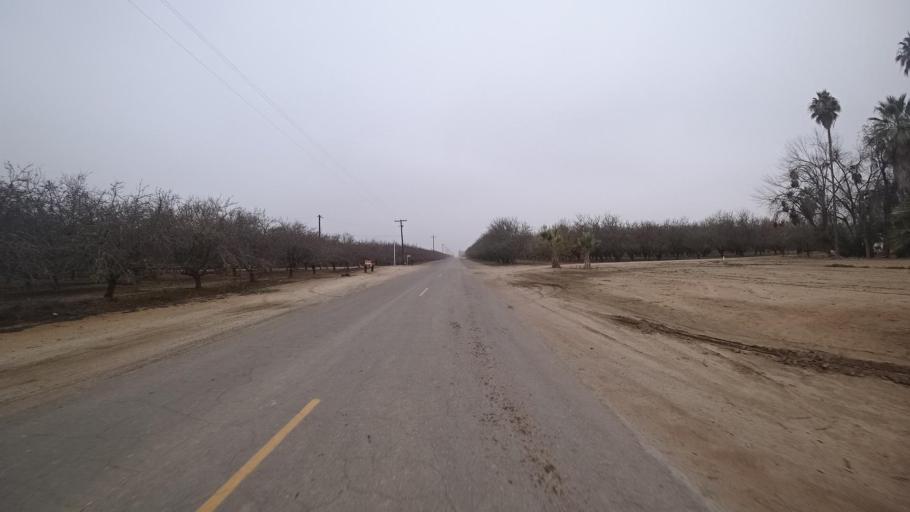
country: US
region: California
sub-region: Kern County
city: Wasco
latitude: 35.5896
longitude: -119.5093
